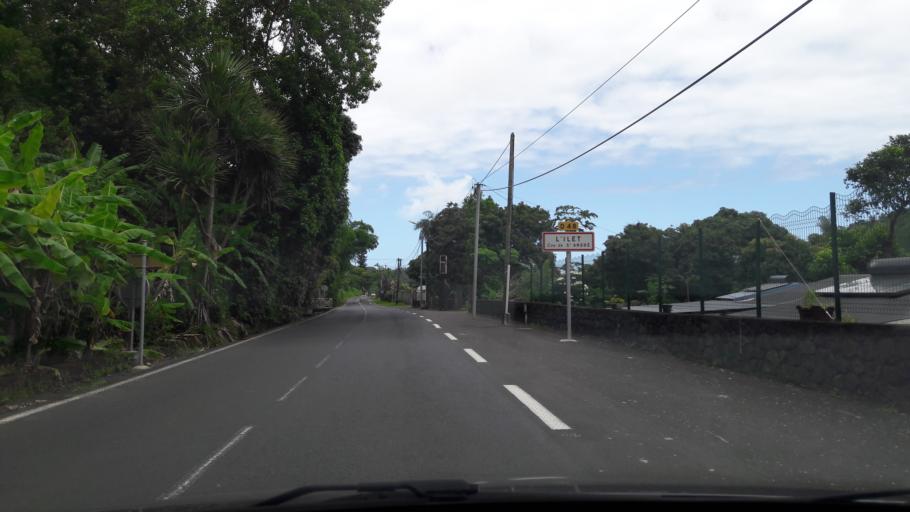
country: RE
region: Reunion
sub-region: Reunion
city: Saint-Andre
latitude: -20.9846
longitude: 55.6264
